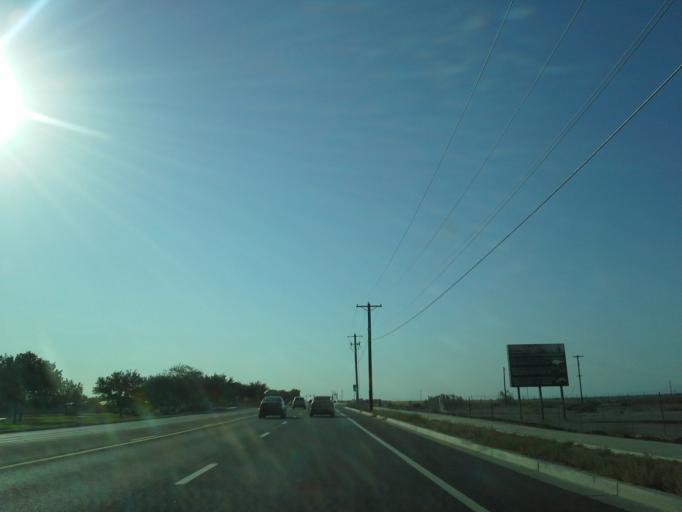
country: US
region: Arizona
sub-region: Pinal County
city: San Tan Valley
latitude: 33.1868
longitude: -111.5945
